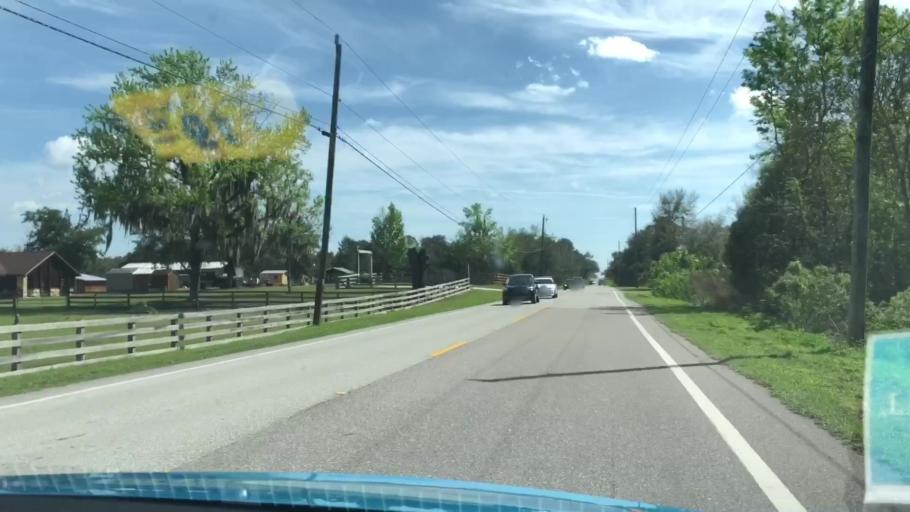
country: US
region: Florida
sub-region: Volusia County
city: Deltona
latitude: 28.8618
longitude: -81.2048
